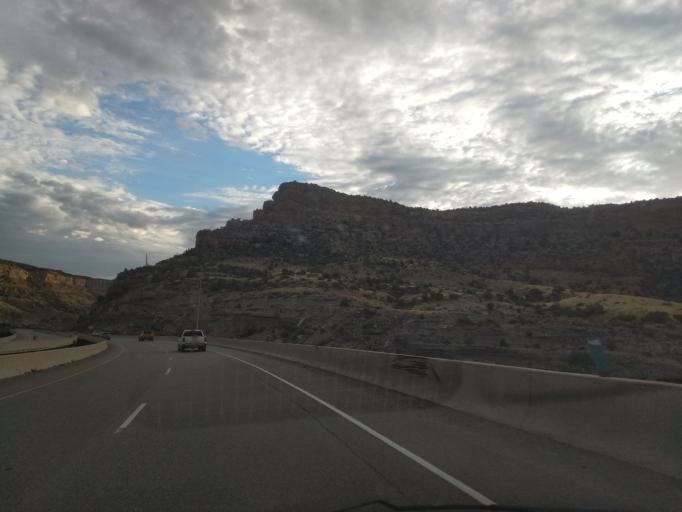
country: US
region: Colorado
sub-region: Mesa County
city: Palisade
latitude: 39.1966
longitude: -108.2684
